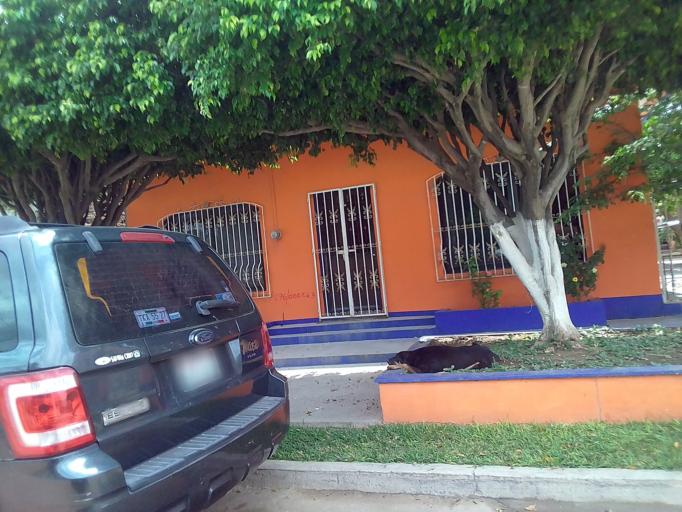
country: MX
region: Oaxaca
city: Union Hidalgo
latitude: 16.4765
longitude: -94.8260
